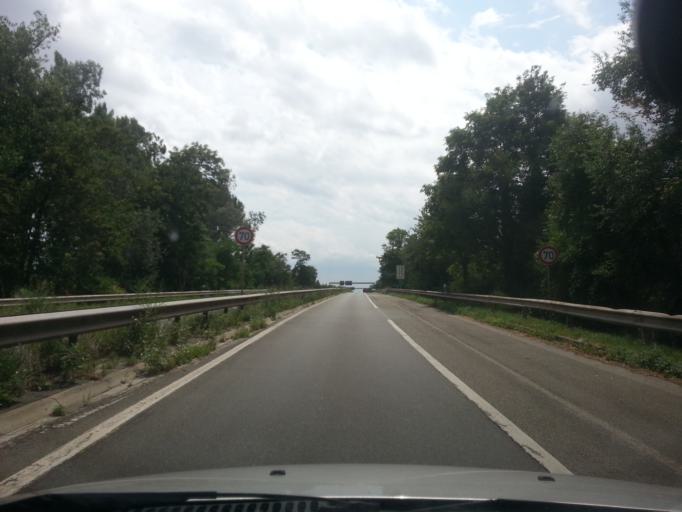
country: DE
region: Rheinland-Pfalz
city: Frankenthal
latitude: 49.5367
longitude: 8.3661
